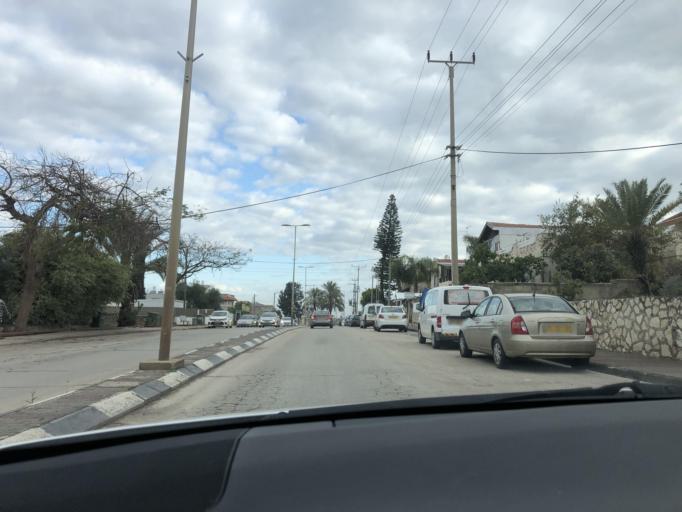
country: IL
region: Central District
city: Rosh Ha'Ayin
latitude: 32.0911
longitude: 34.9540
